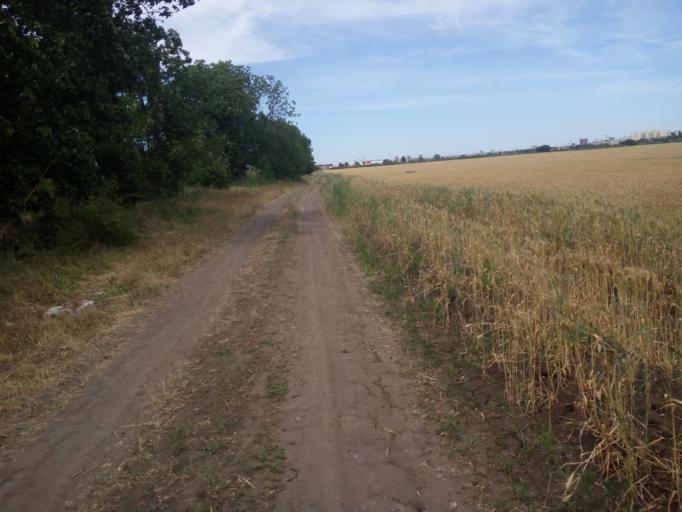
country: RU
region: Rostov
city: Bataysk
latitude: 47.1144
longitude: 39.7230
